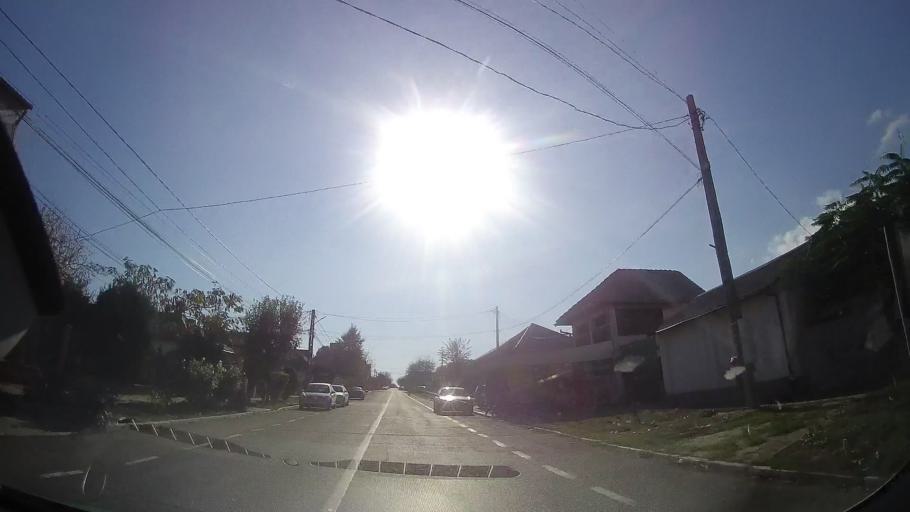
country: RO
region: Constanta
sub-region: Comuna Costinesti
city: Schitu
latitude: 43.9424
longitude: 28.6294
